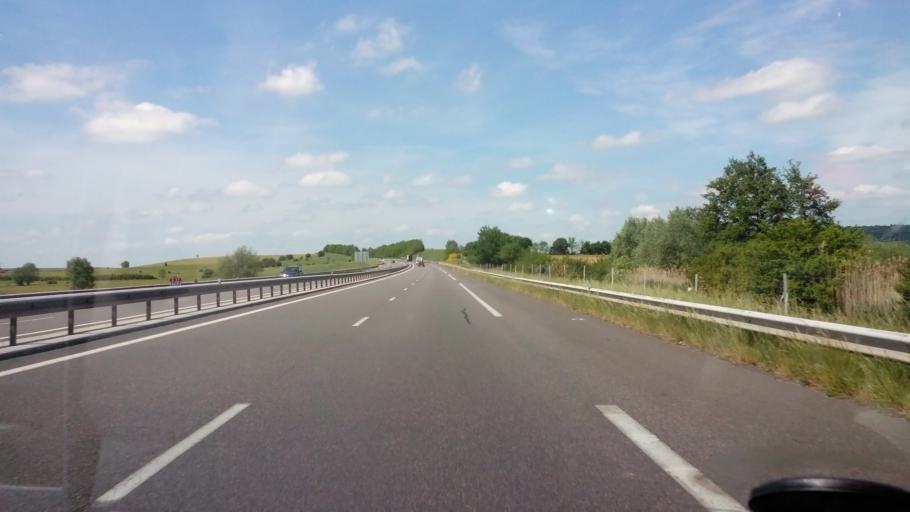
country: FR
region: Lorraine
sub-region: Departement des Vosges
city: Bulgneville
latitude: 48.1922
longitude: 5.7716
